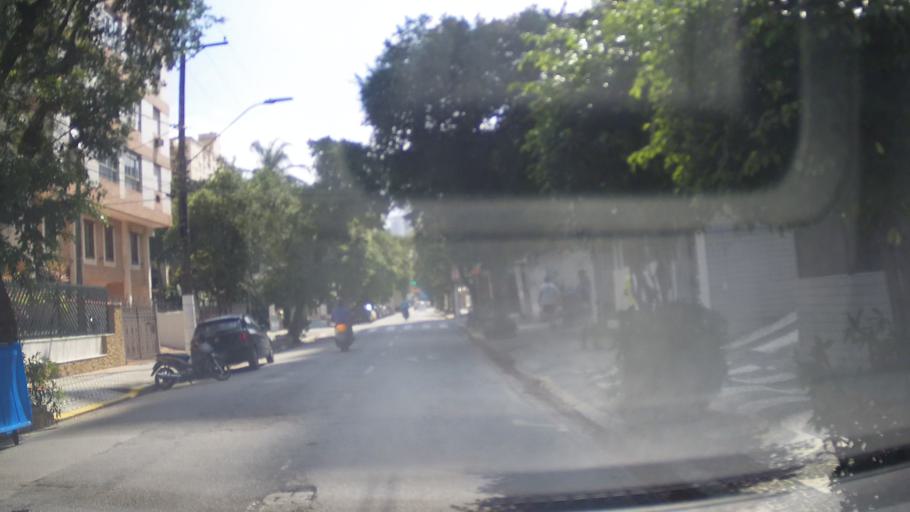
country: BR
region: Sao Paulo
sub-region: Santos
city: Santos
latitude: -23.9650
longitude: -46.3427
